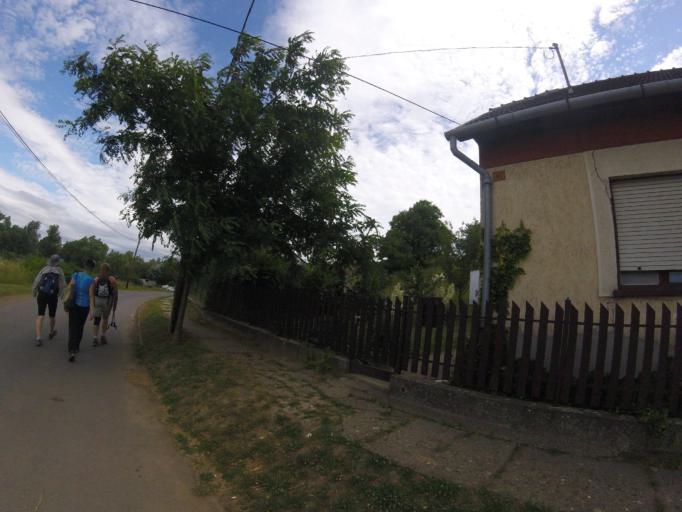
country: HU
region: Nograd
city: Romhany
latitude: 47.9185
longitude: 19.2546
